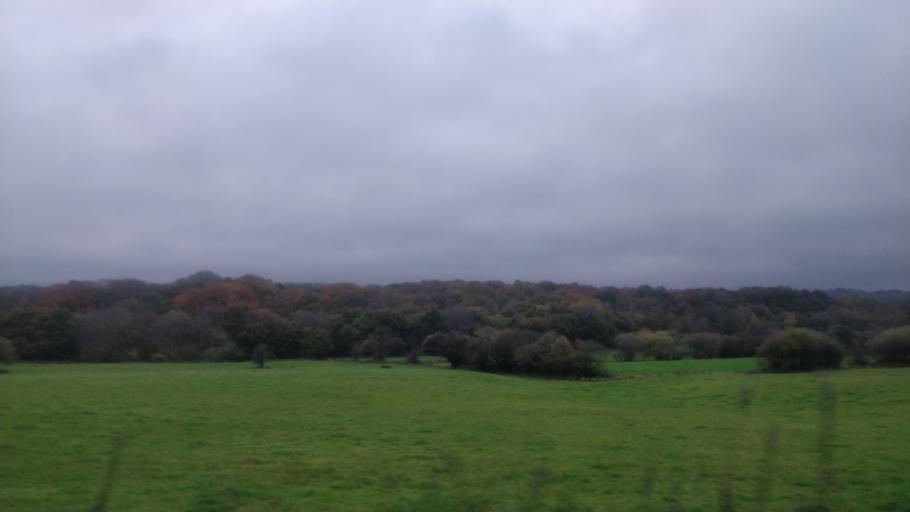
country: GB
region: England
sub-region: Borough of Wigan
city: Shevington
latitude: 53.5587
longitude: -2.6883
